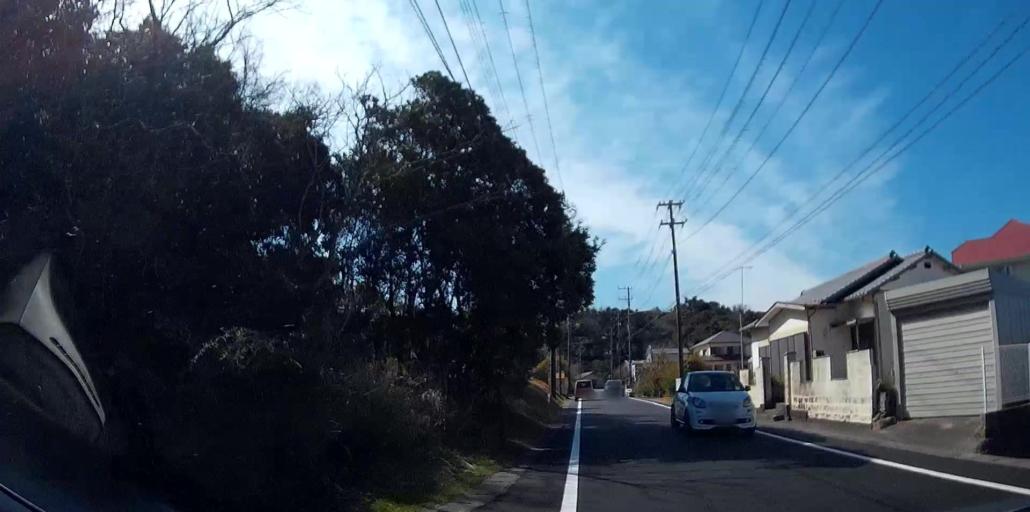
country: JP
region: Chiba
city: Tateyama
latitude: 35.0348
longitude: 139.8500
